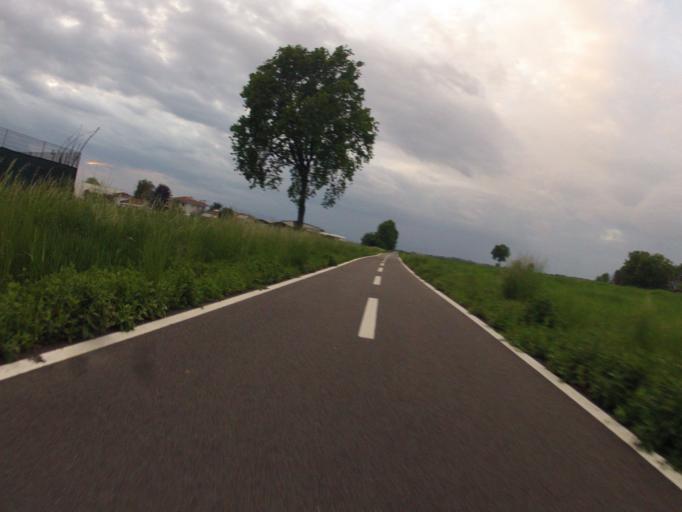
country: IT
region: Piedmont
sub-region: Provincia di Torino
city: Villafranca Piemonte
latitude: 44.7891
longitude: 7.5090
